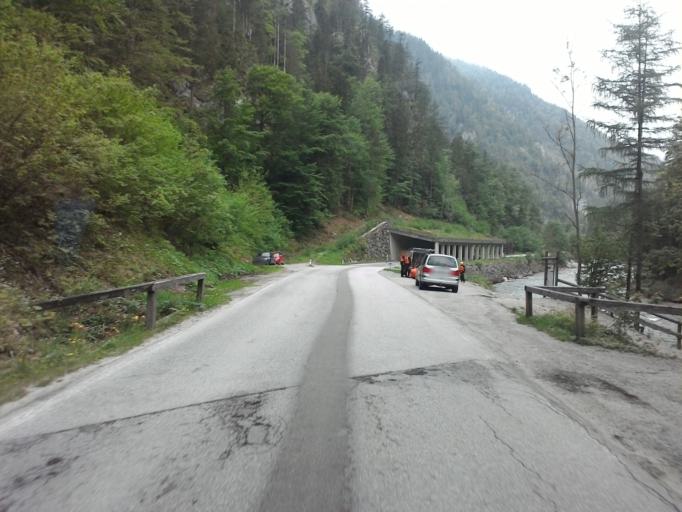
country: AT
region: Styria
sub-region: Politischer Bezirk Liezen
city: Palfau
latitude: 47.6875
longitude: 14.8865
